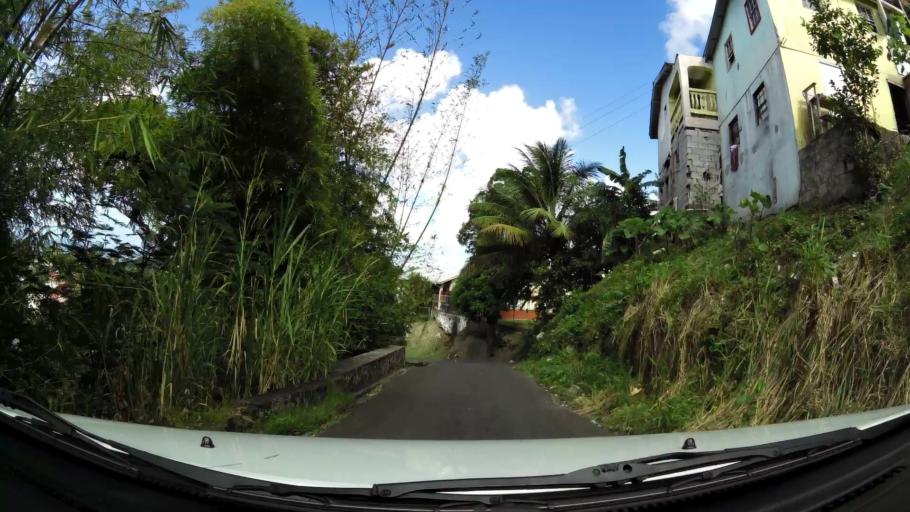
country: LC
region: Castries Quarter
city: Bisee
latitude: 14.0112
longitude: -60.9789
